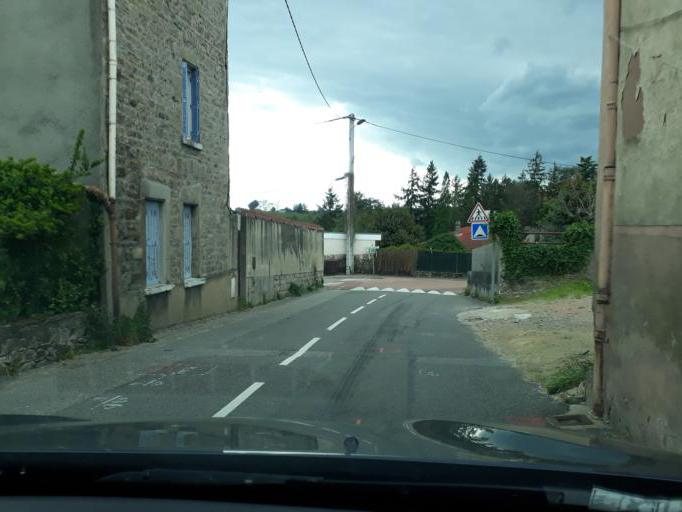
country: FR
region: Rhone-Alpes
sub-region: Departement du Rhone
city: Soucieu-en-Jarrest
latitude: 45.6778
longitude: 4.7059
